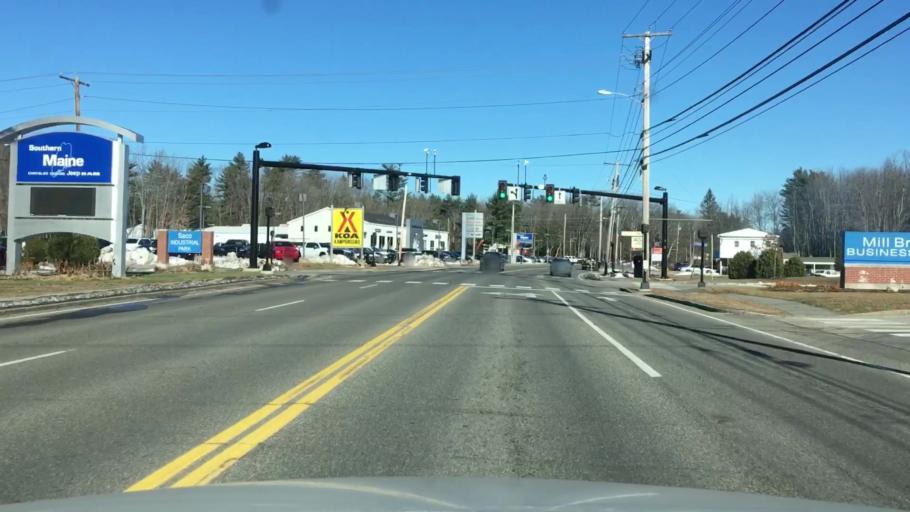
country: US
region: Maine
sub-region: York County
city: Saco
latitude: 43.5329
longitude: -70.4249
